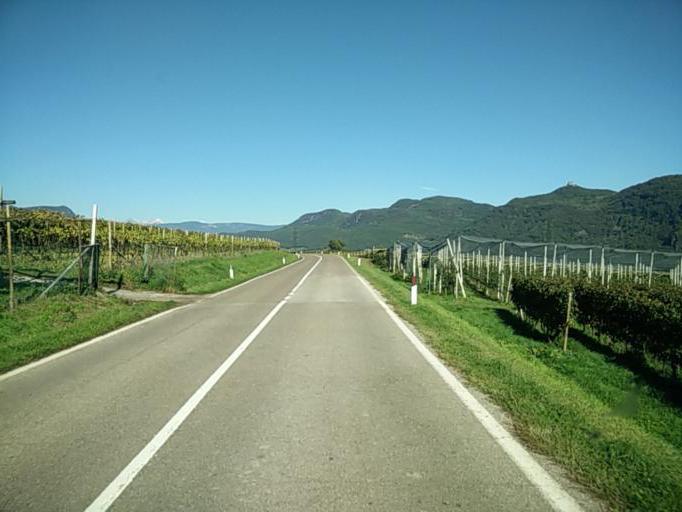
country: IT
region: Trentino-Alto Adige
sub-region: Bolzano
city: Termeno
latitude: 46.3594
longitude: 11.2531
